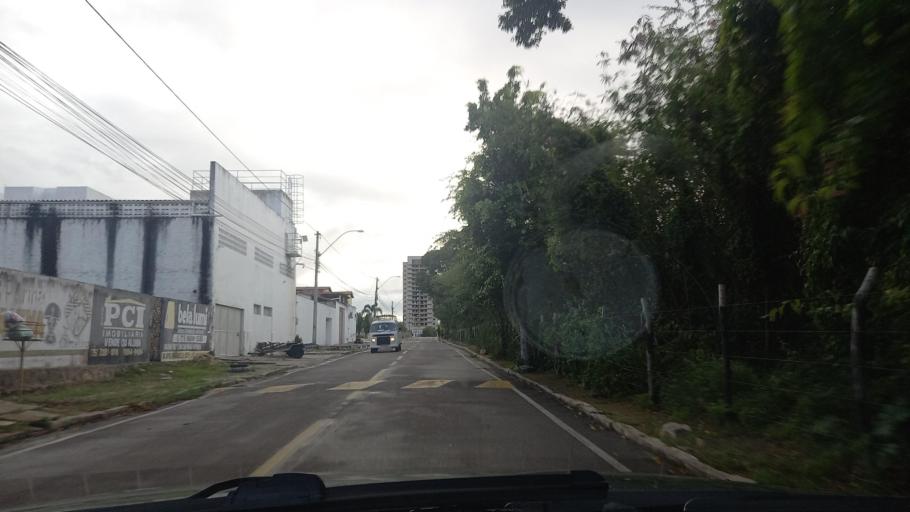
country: BR
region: Bahia
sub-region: Paulo Afonso
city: Paulo Afonso
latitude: -9.3977
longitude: -38.2284
